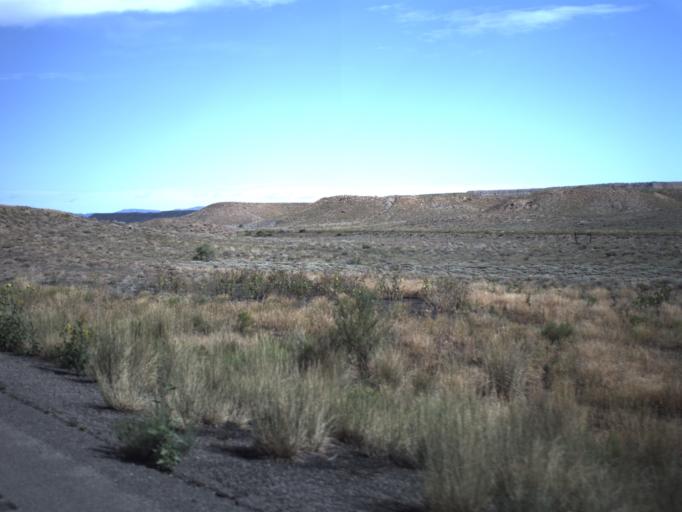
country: US
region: Utah
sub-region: Carbon County
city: East Carbon City
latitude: 39.4621
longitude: -110.4886
